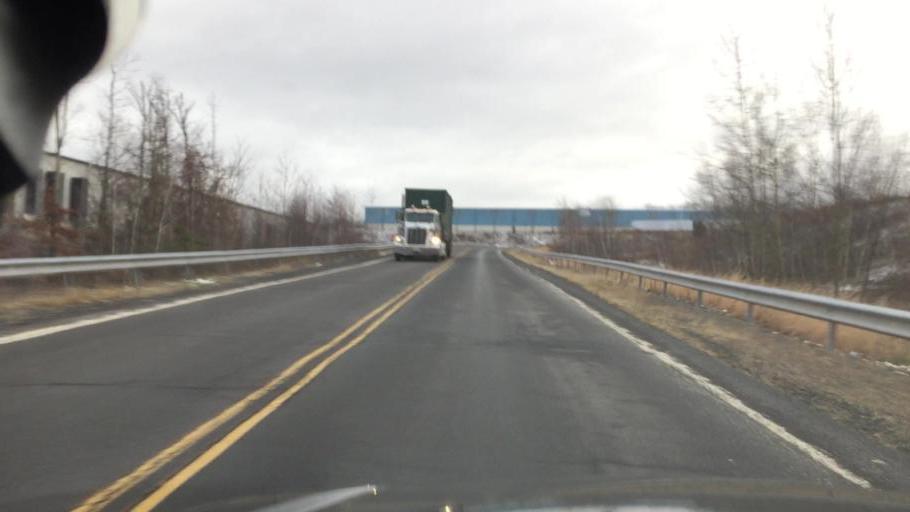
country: US
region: Pennsylvania
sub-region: Luzerne County
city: Mountain Top
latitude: 41.1329
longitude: -75.9008
